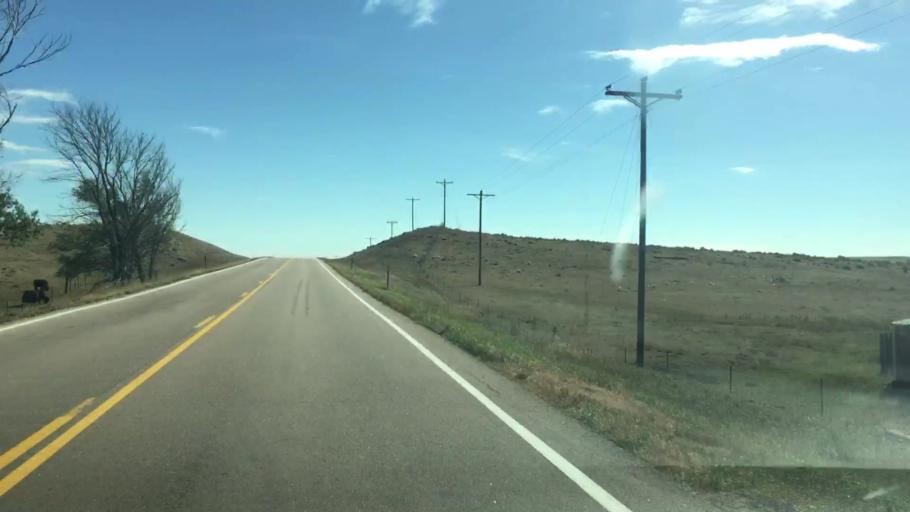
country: US
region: Colorado
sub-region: Elbert County
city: Kiowa
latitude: 39.2736
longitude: -104.1563
